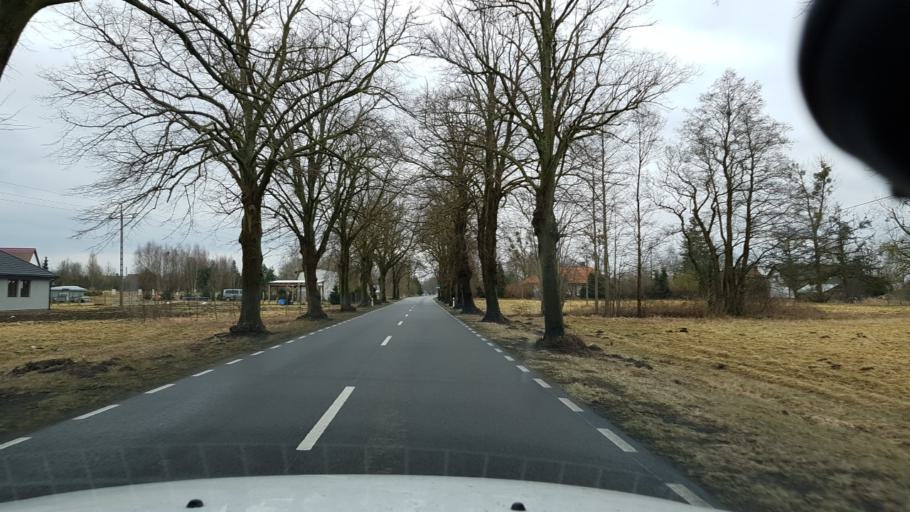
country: PL
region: West Pomeranian Voivodeship
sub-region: Powiat goleniowski
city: Goleniow
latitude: 53.5995
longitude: 14.7399
